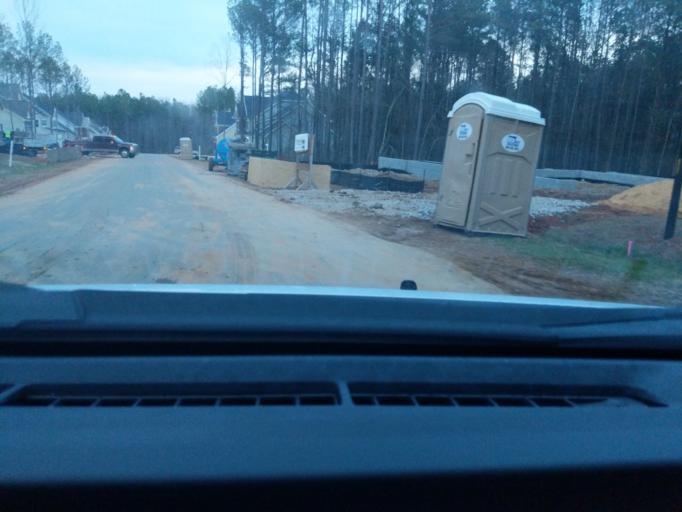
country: US
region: North Carolina
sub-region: Wake County
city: Garner
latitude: 35.7097
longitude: -78.6832
